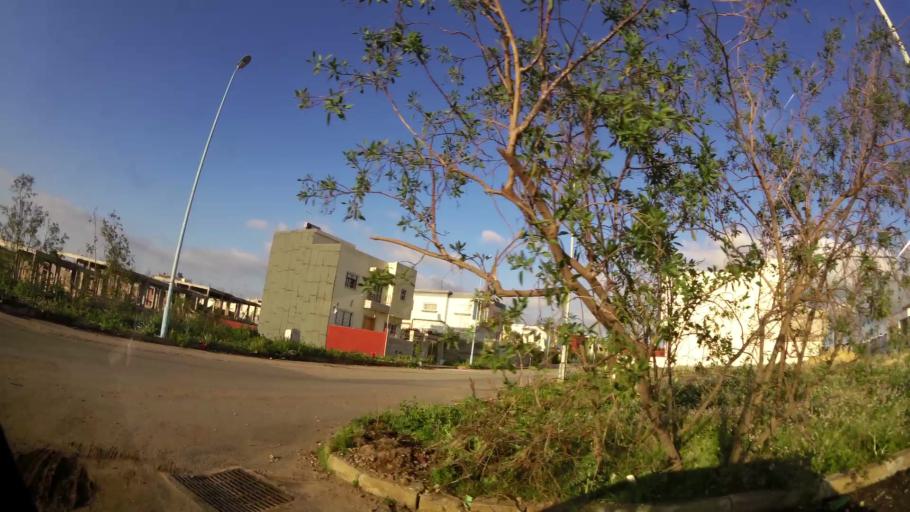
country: MA
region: Chaouia-Ouardigha
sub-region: Settat Province
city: Settat
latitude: 33.0132
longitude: -7.6010
